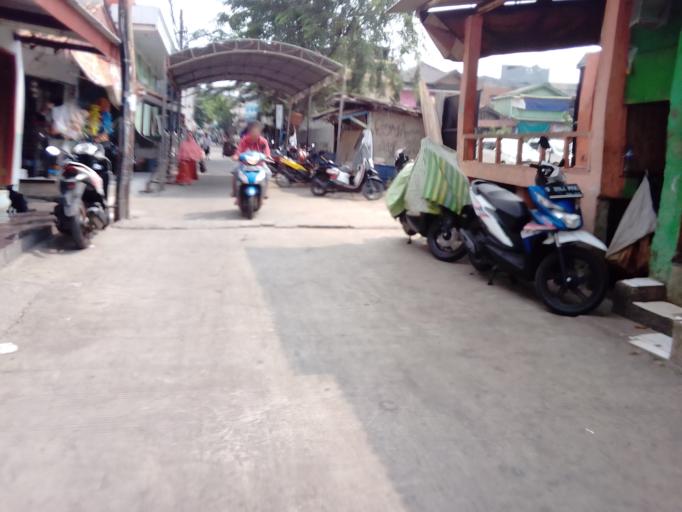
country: ID
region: Jakarta Raya
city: Jakarta
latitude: -6.1941
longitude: 106.8087
